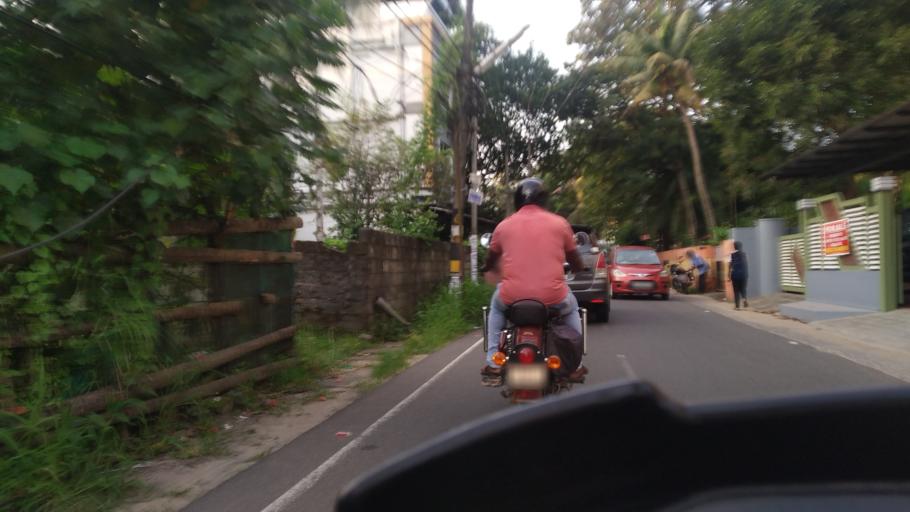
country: IN
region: Kerala
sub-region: Ernakulam
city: Elur
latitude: 10.0220
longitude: 76.3005
